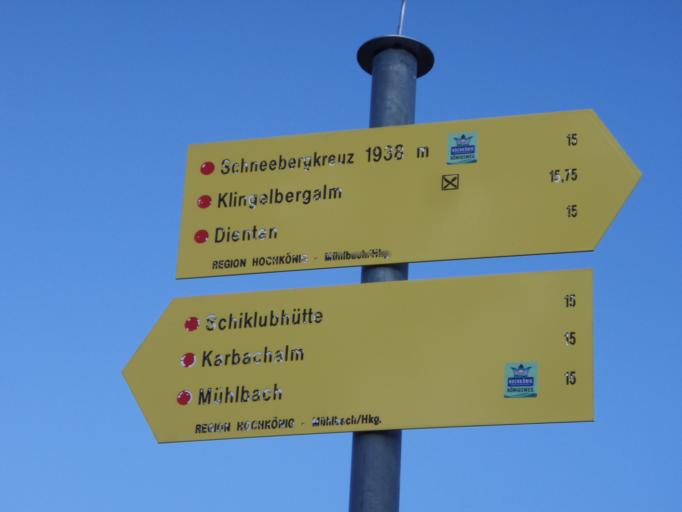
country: AT
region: Salzburg
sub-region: Politischer Bezirk Sankt Johann im Pongau
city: Goldegg
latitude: 47.3688
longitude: 13.0729
